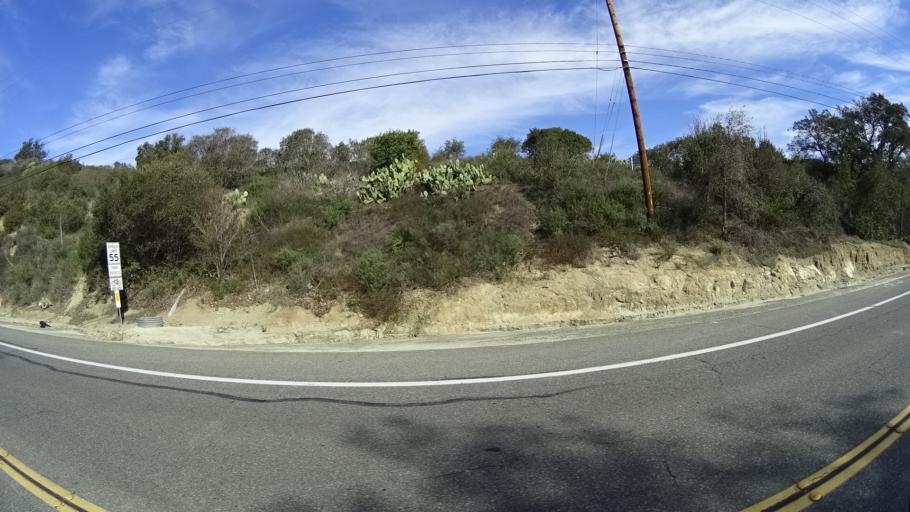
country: US
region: California
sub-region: Orange County
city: Portola Hills
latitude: 33.6978
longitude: -117.6343
